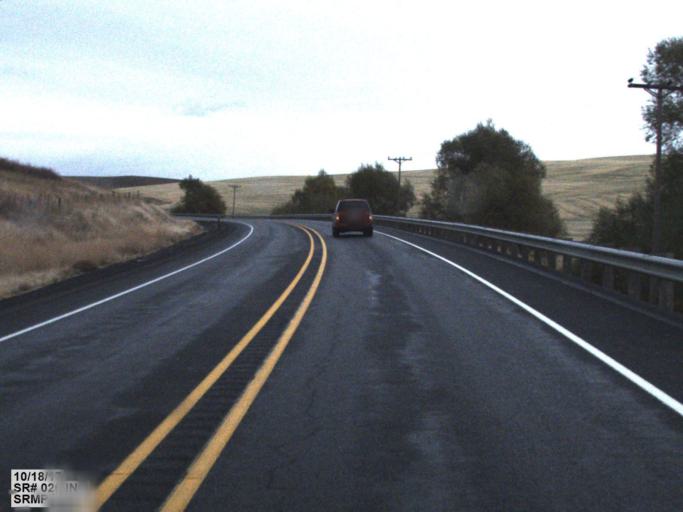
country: US
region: Washington
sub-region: Whitman County
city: Colfax
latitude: 46.8338
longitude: -117.4987
